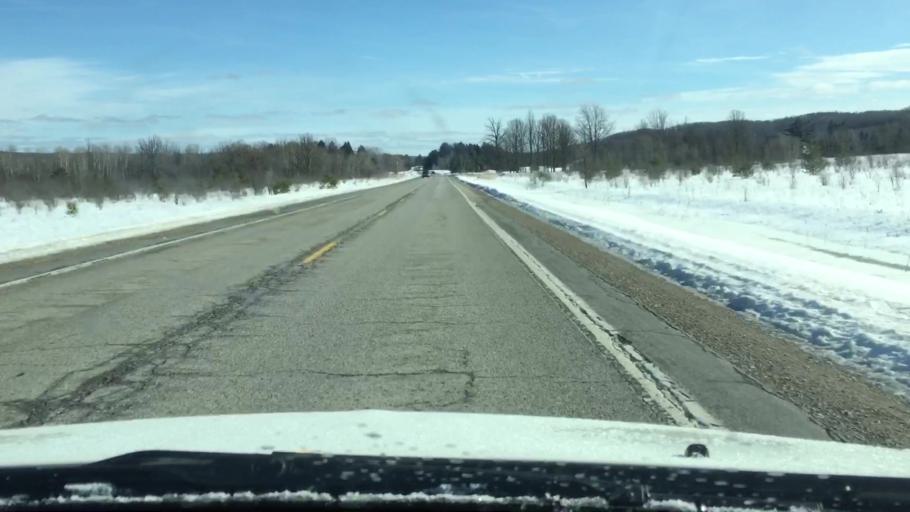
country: US
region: Michigan
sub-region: Charlevoix County
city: East Jordan
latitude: 45.1023
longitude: -85.1173
